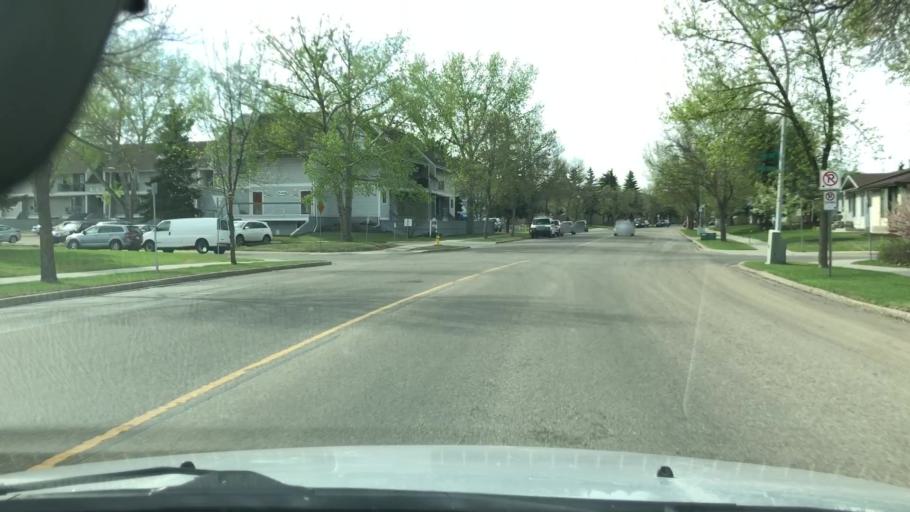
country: CA
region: Alberta
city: Edmonton
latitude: 53.6014
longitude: -113.5280
